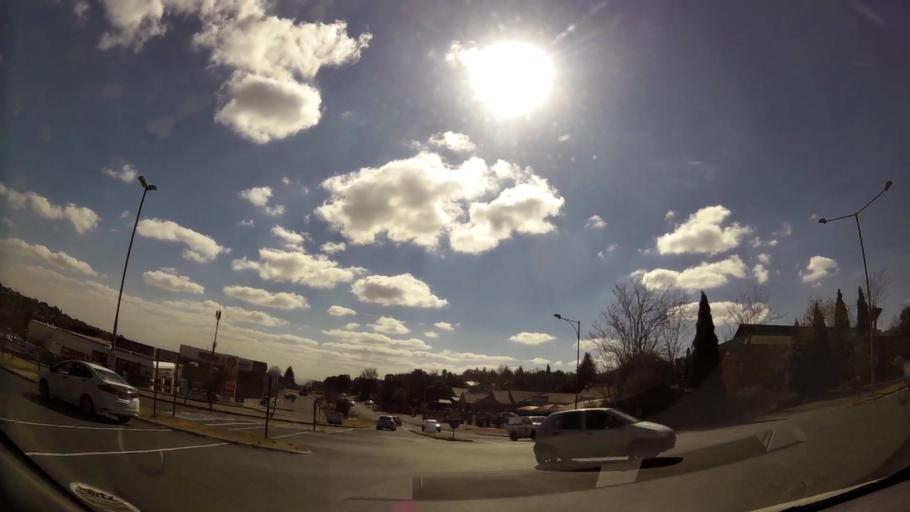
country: ZA
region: Gauteng
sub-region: West Rand District Municipality
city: Krugersdorp
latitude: -26.0976
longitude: 27.8038
